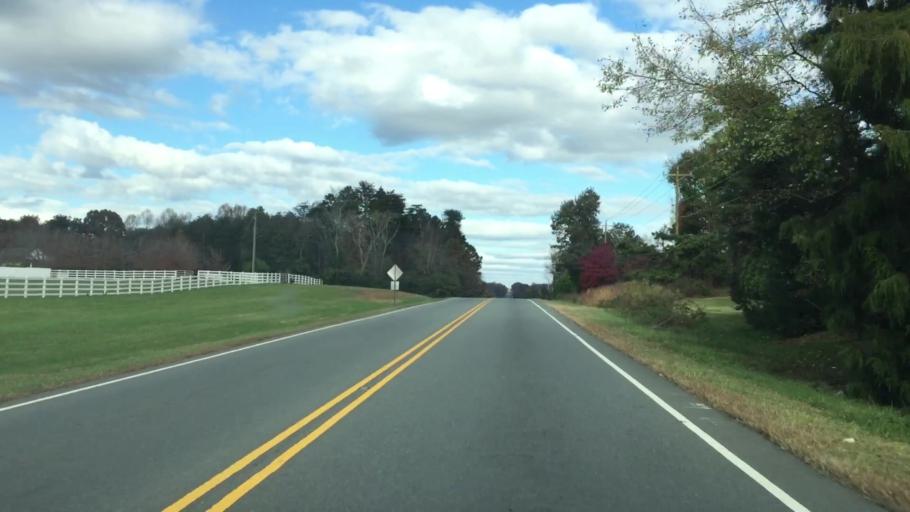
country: US
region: North Carolina
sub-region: Forsyth County
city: Walkertown
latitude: 36.1374
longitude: -80.1651
